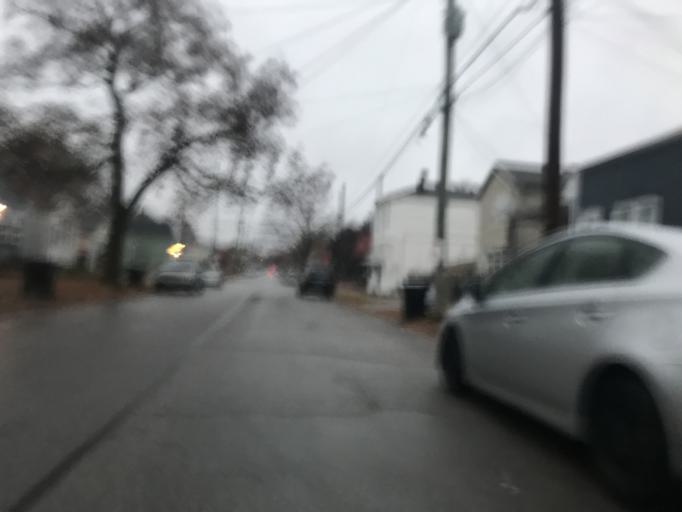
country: US
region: Kentucky
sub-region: Jefferson County
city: Louisville
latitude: 38.2313
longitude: -85.7433
